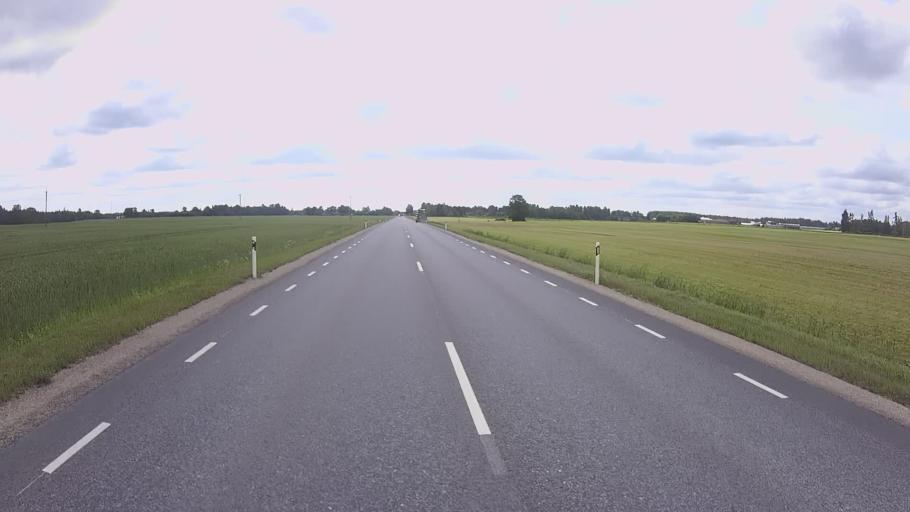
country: EE
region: Polvamaa
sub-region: Polva linn
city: Polva
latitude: 58.0792
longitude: 27.0384
